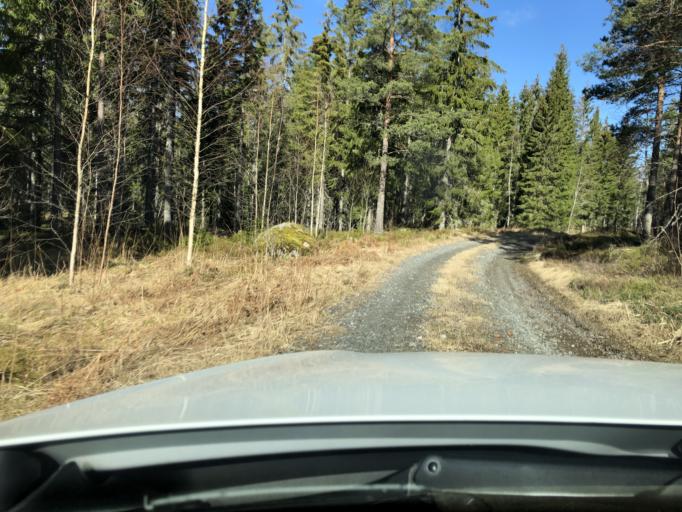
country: SE
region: Uppsala
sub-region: Heby Kommun
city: OEstervala
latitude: 60.3272
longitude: 17.1742
